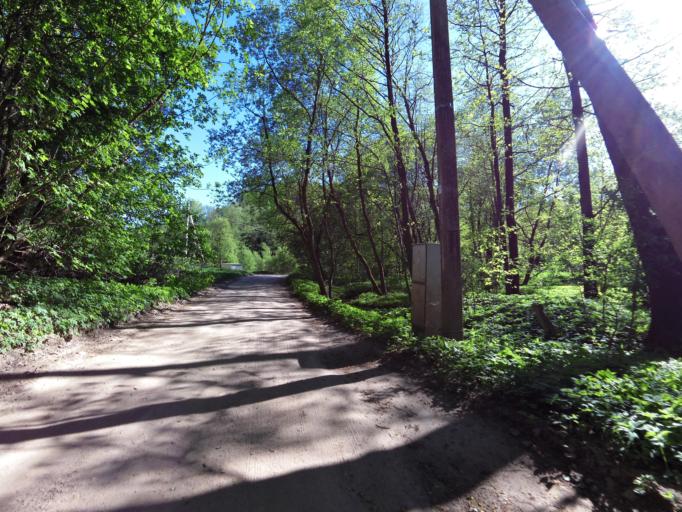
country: LT
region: Vilnius County
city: Pilaite
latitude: 54.6875
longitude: 25.1556
